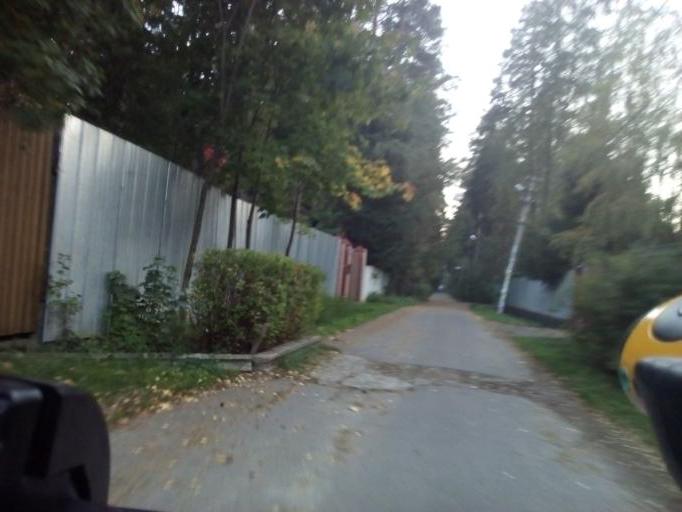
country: RU
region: Moskovskaya
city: Kratovo
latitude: 55.5943
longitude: 38.1917
